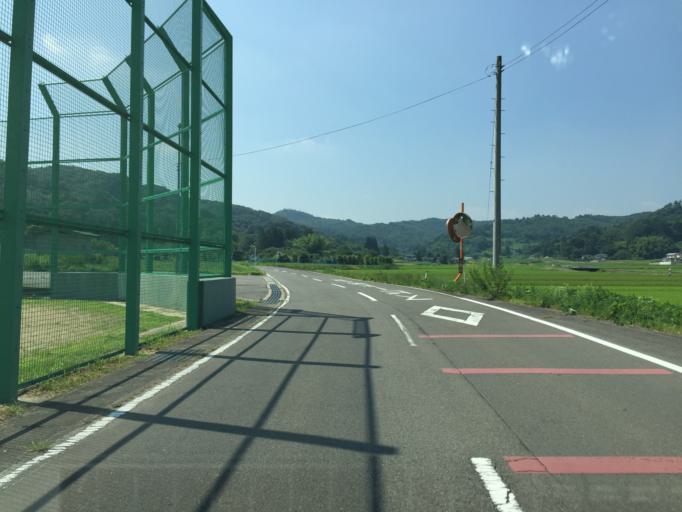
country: JP
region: Fukushima
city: Fukushima-shi
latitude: 37.7004
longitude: 140.4463
